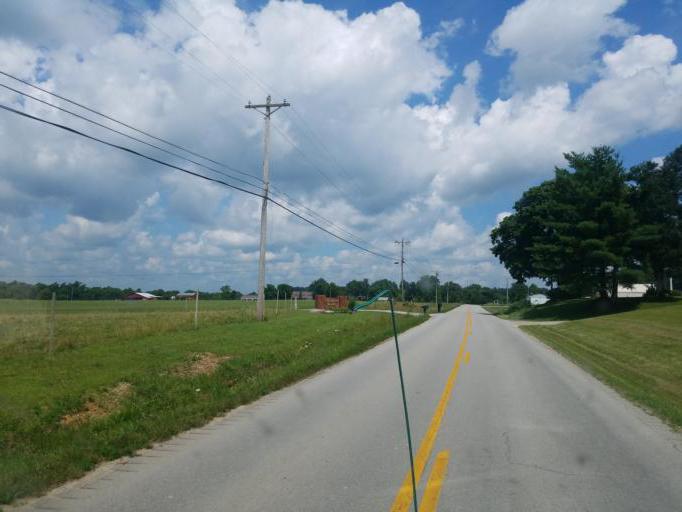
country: US
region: Kentucky
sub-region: Grayson County
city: Leitchfield
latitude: 37.5159
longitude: -86.3280
